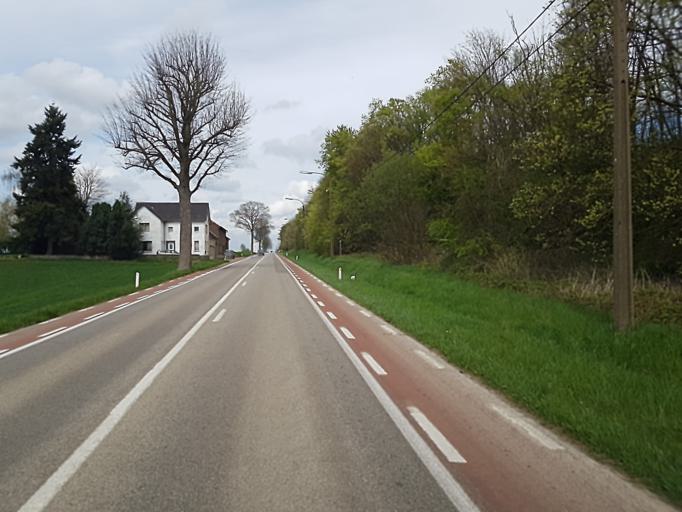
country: BE
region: Flanders
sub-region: Provincie Limburg
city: Riemst
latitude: 50.8492
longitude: 5.6253
